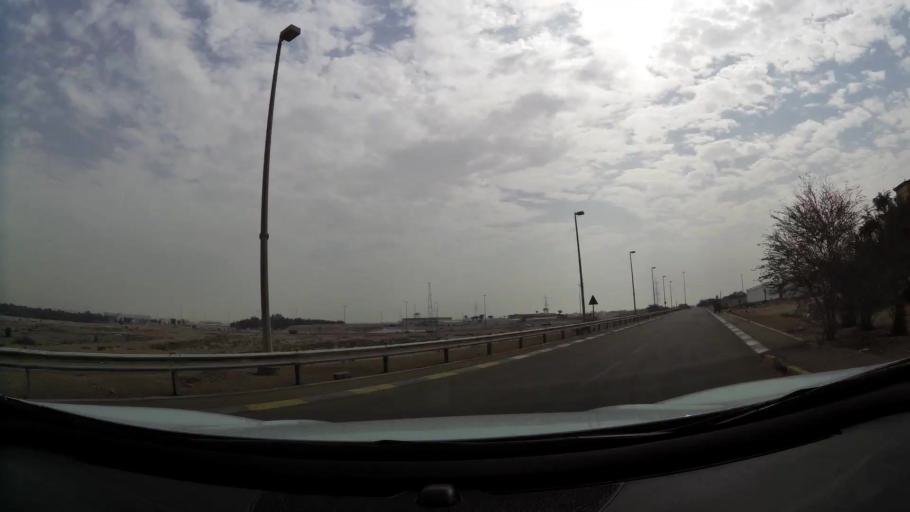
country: AE
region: Abu Dhabi
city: Abu Dhabi
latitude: 24.3003
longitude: 54.6623
